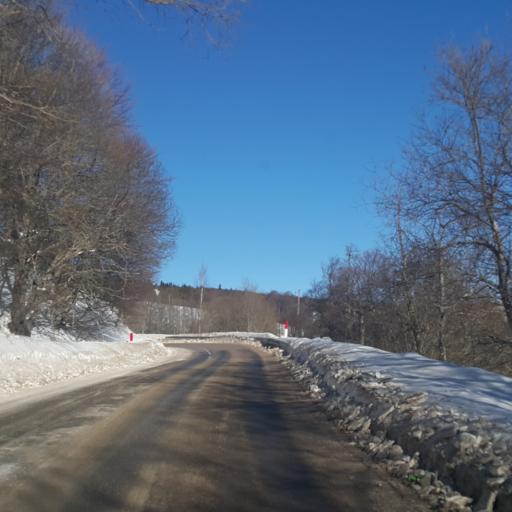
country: XK
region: Mitrovica
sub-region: Komuna e Leposaviqit
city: Leposaviq
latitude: 43.3158
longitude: 20.8492
